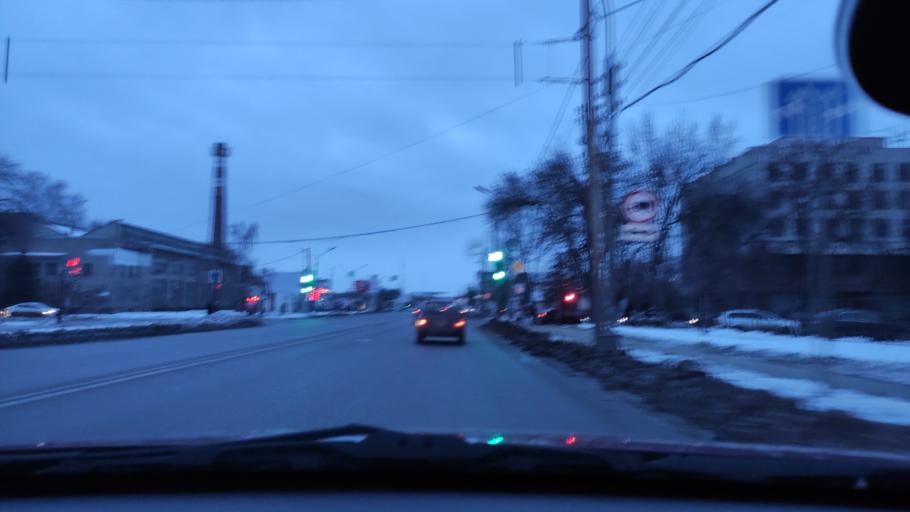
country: RU
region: Tambov
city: Tambov
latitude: 52.7211
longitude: 41.4376
